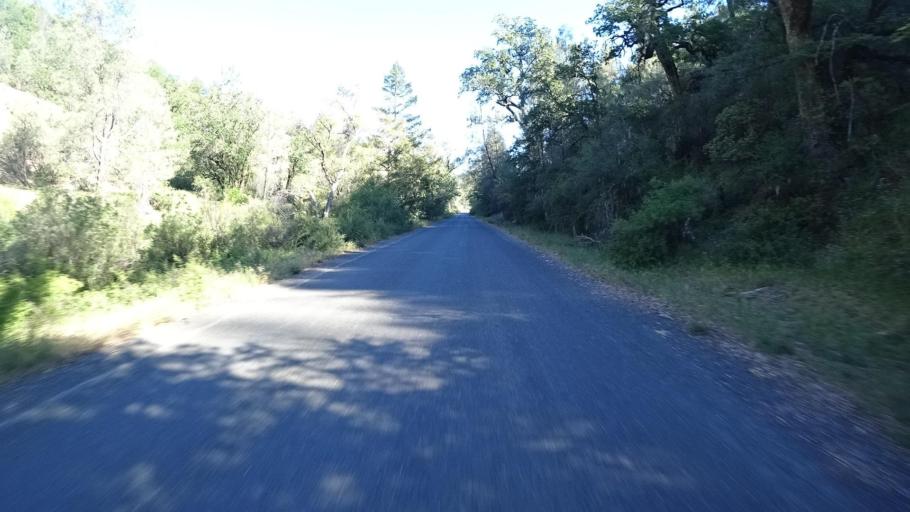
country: US
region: California
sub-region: Lake County
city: Upper Lake
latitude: 39.4182
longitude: -122.9784
